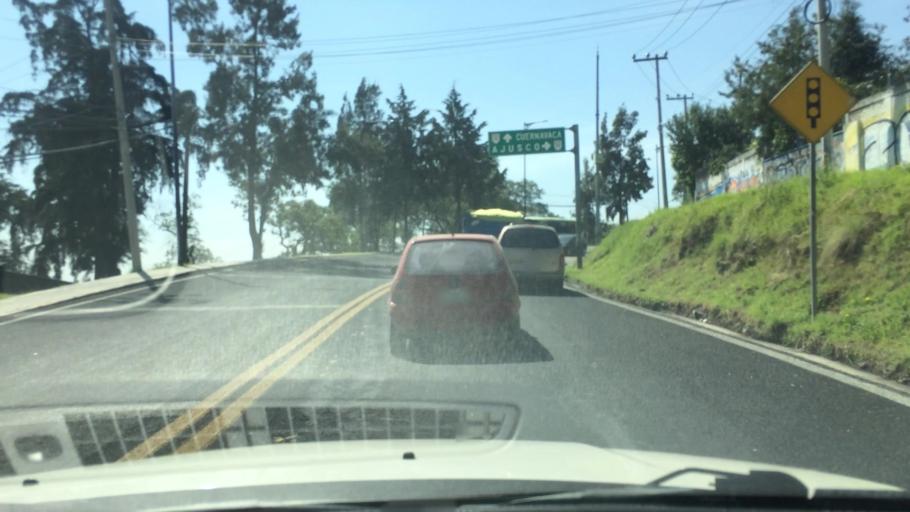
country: MX
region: Mexico City
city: Xochimilco
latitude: 19.2359
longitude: -99.1582
